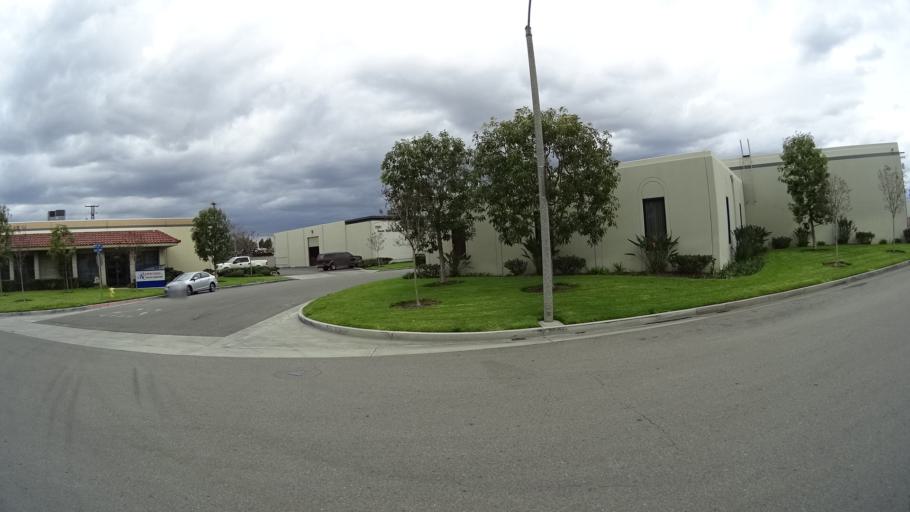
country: US
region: California
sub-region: Orange County
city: Placentia
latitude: 33.8498
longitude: -117.8670
